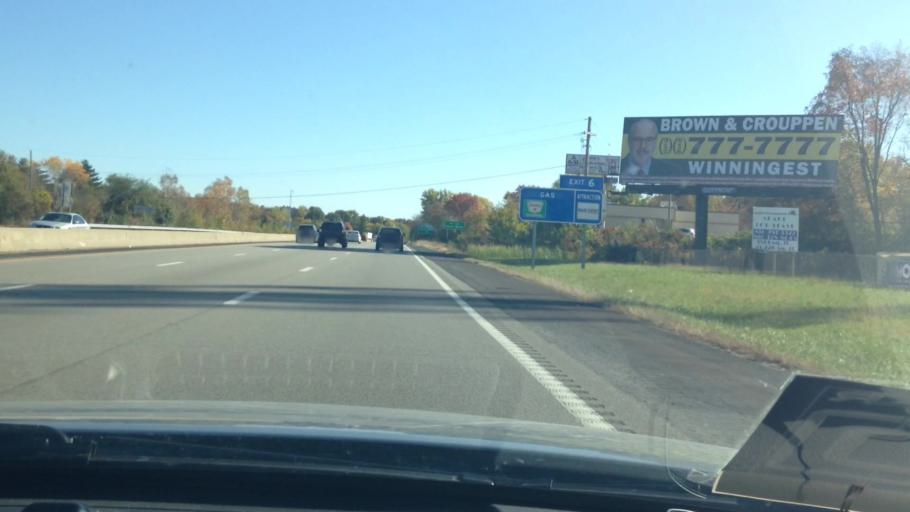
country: US
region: Missouri
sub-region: Platte County
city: Weatherby Lake
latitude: 39.2337
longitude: -94.6562
